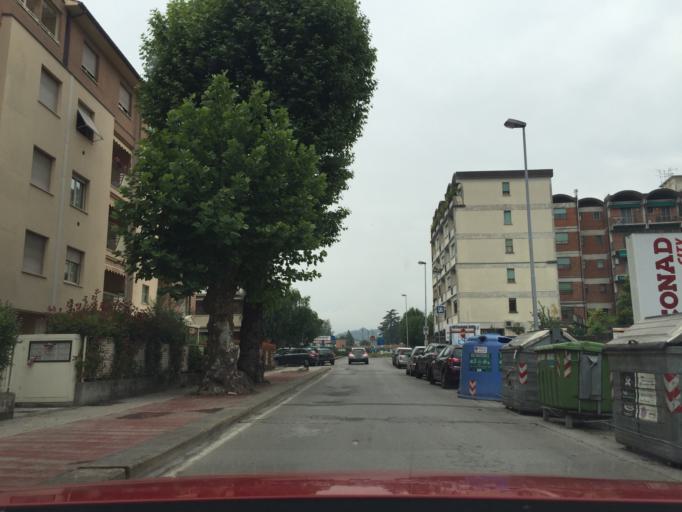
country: IT
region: Tuscany
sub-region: Provincia di Pistoia
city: Pistoia
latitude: 43.9392
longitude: 10.9137
